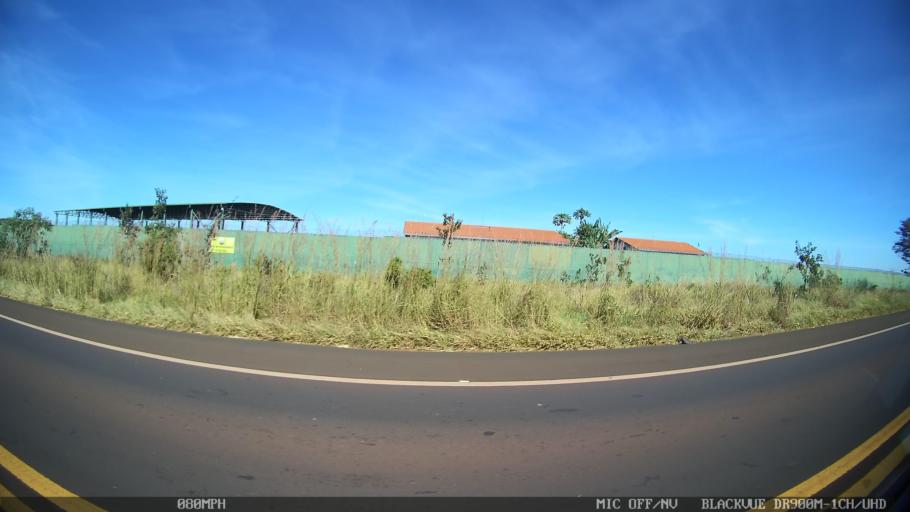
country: BR
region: Sao Paulo
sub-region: Franca
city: Franca
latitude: -20.5569
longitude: -47.5617
